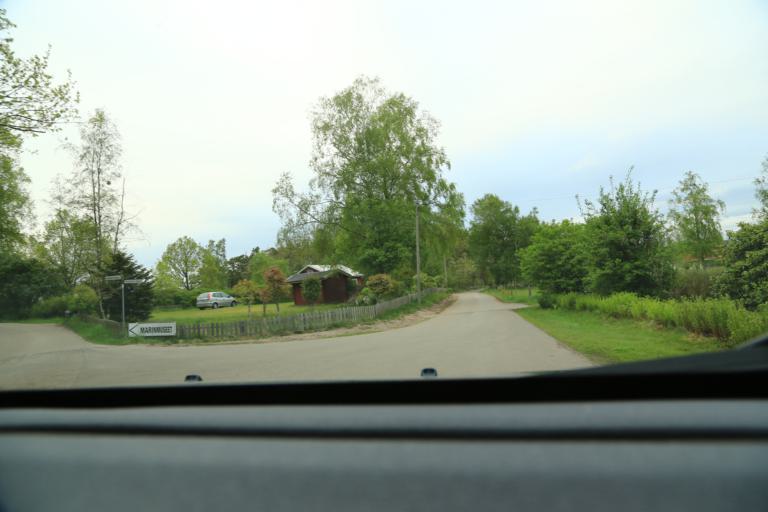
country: SE
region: Halland
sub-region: Varbergs Kommun
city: Varberg
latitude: 57.1489
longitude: 12.2275
